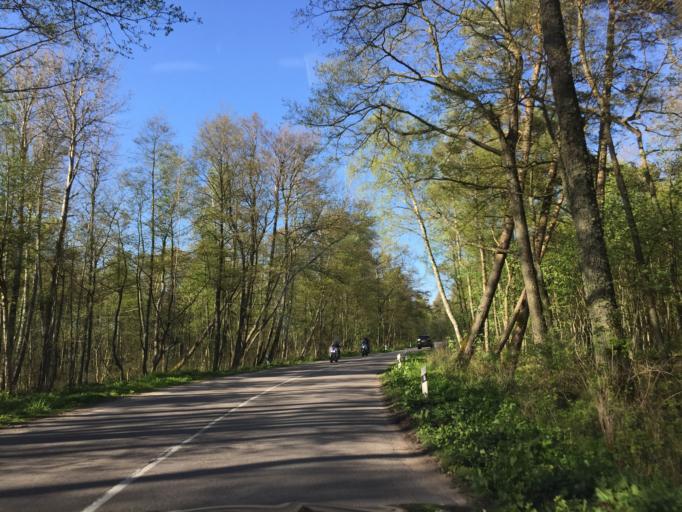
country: LT
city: Nida
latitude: 55.2001
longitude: 20.8685
